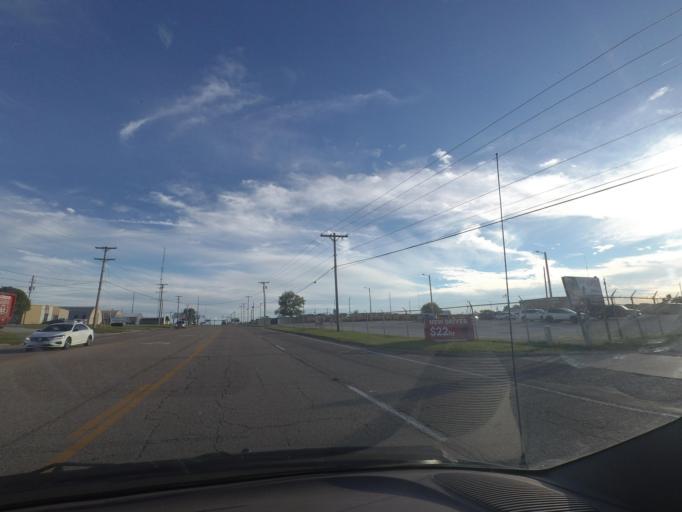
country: US
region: Illinois
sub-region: Sangamon County
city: Grandview
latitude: 39.7972
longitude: -89.6060
